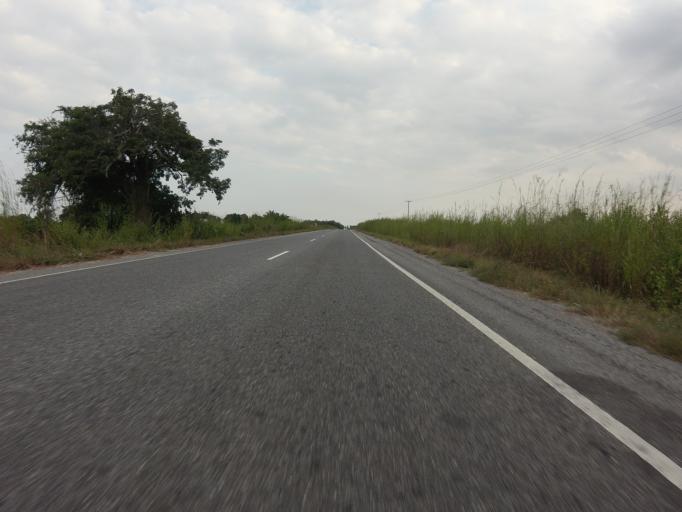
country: GH
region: Volta
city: Ho
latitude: 6.2420
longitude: 0.5510
